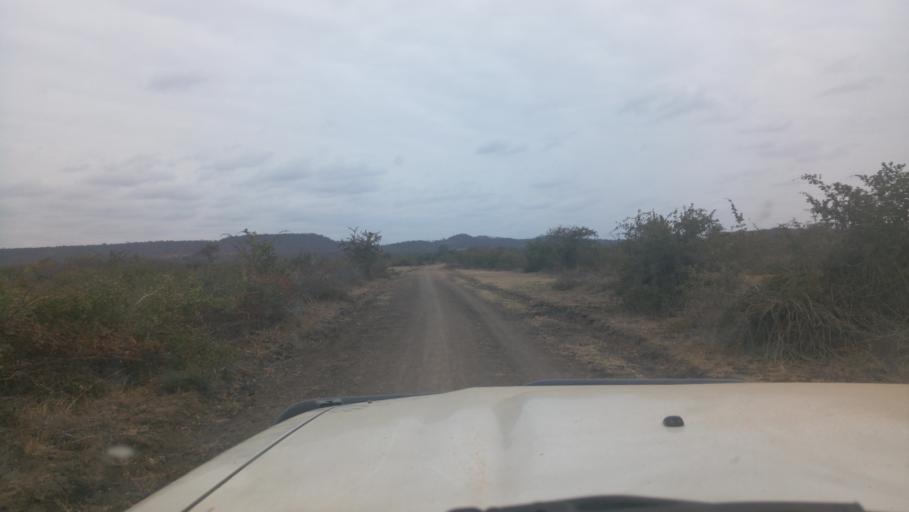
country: KE
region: Makueni
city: Makueni
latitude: -2.0255
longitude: 38.0979
